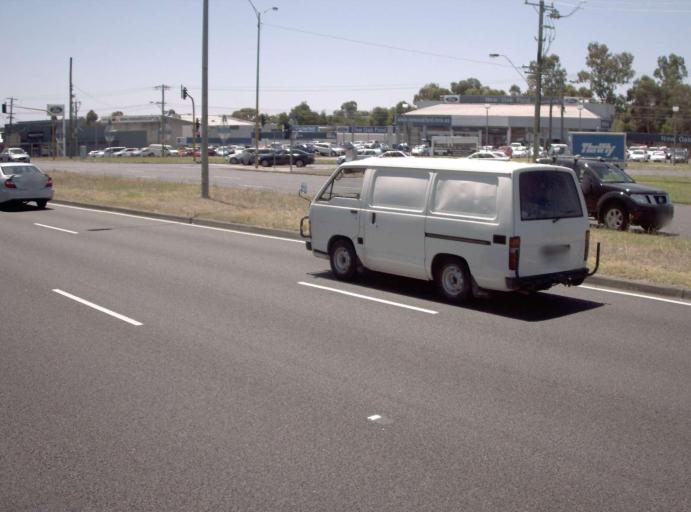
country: AU
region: Victoria
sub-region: Monash
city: Chadstone
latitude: -37.8969
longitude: 145.0989
